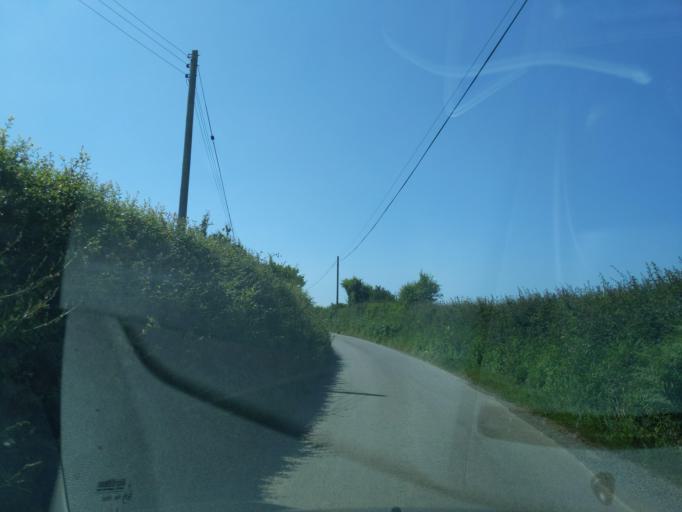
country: GB
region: England
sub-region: Cornwall
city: Wadebridge
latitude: 50.5839
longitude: -4.8454
